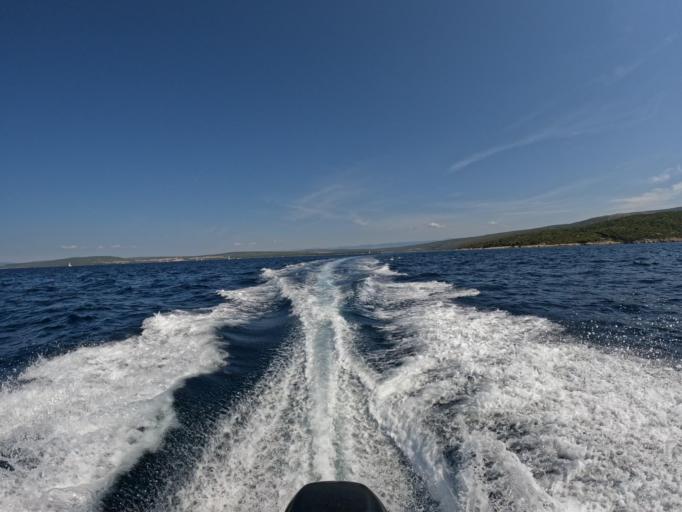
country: HR
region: Primorsko-Goranska
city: Punat
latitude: 44.9752
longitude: 14.6090
